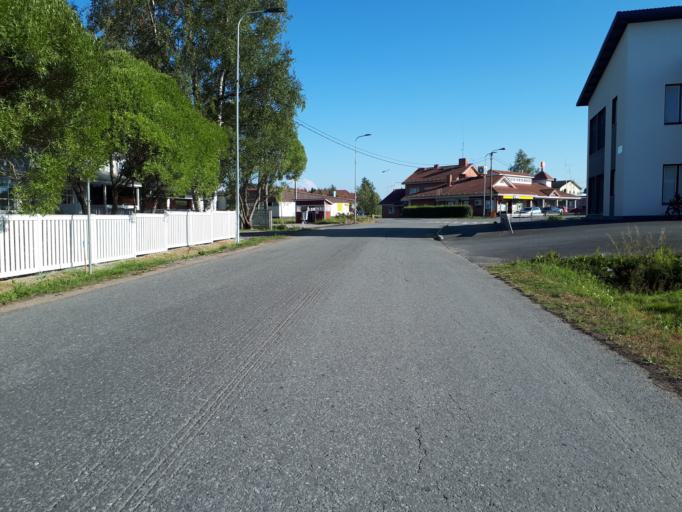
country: FI
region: Northern Ostrobothnia
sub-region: Oulunkaari
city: Ii
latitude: 65.3240
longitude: 25.3774
